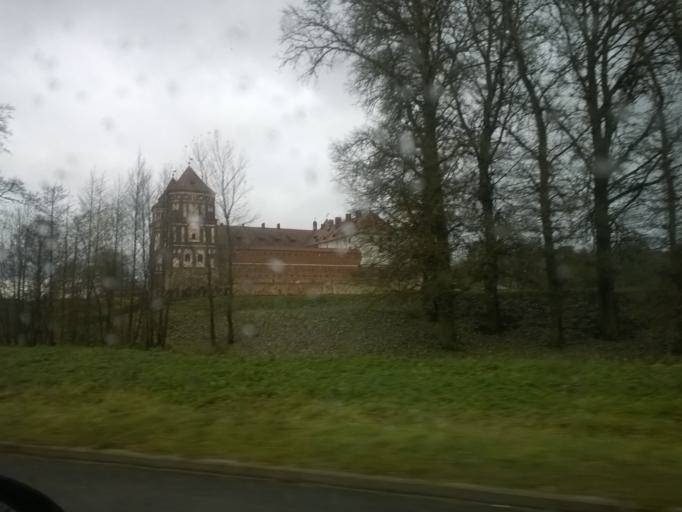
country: BY
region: Grodnenskaya
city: Mir
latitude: 53.4500
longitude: 26.4715
